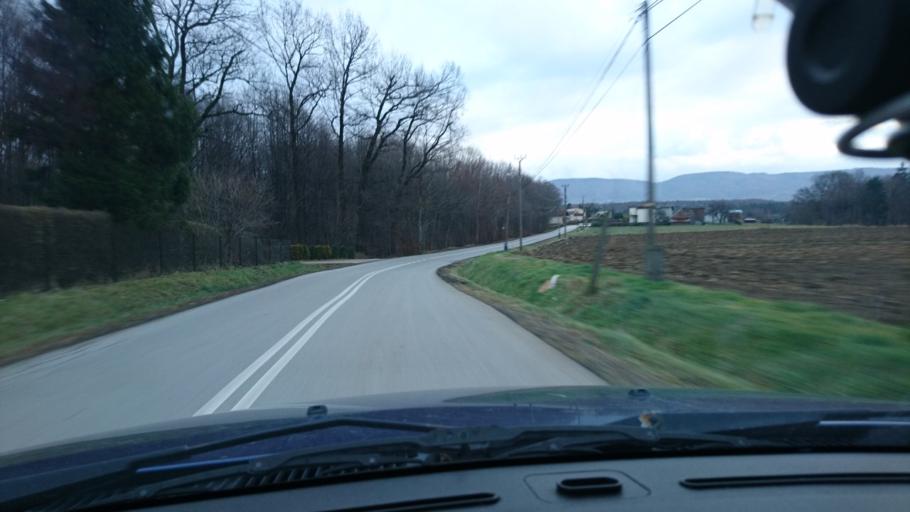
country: PL
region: Silesian Voivodeship
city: Janowice
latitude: 49.8822
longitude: 19.0997
